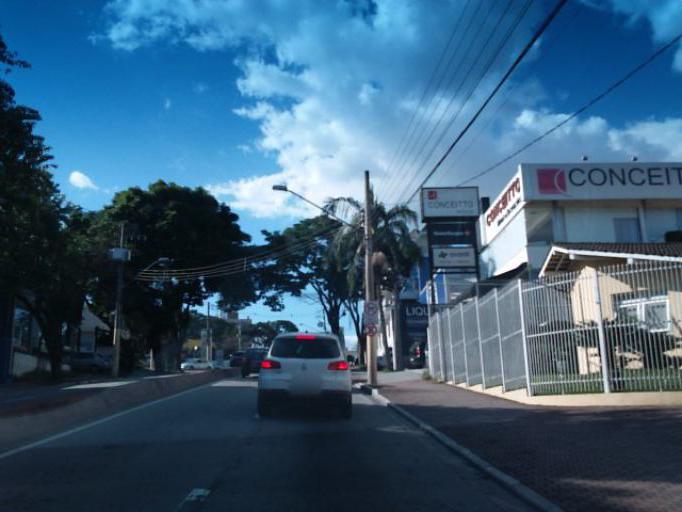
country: BR
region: Sao Paulo
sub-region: Sao Jose Dos Campos
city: Sao Jose dos Campos
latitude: -23.2031
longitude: -45.9039
